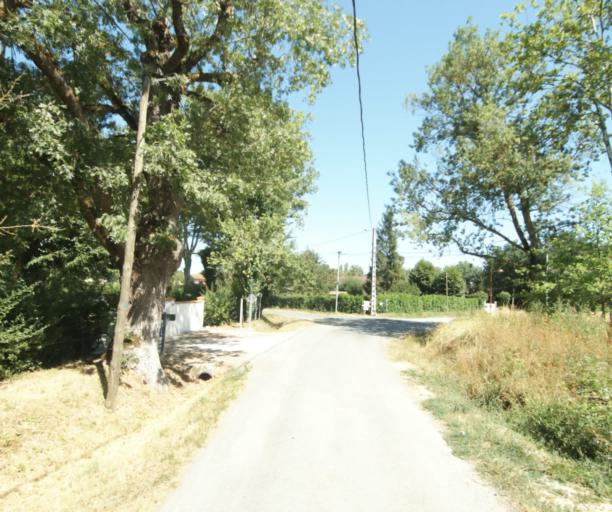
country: FR
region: Midi-Pyrenees
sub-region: Departement de la Haute-Garonne
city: Revel
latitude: 43.4934
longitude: 1.9708
